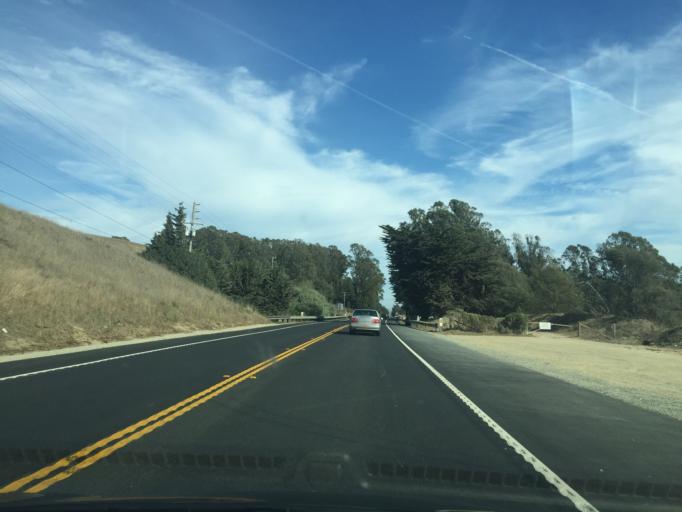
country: US
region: California
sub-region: Santa Cruz County
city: Santa Cruz
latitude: 36.9621
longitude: -122.0724
